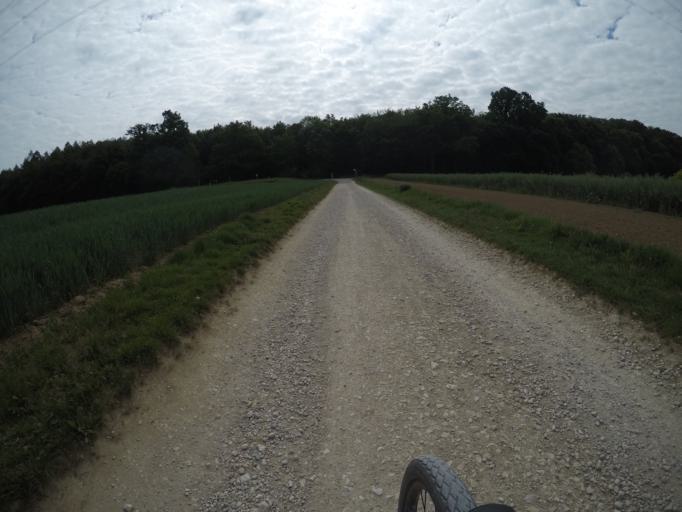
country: DE
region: Baden-Wuerttemberg
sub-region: Regierungsbezirk Stuttgart
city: Oberboihingen
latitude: 48.6503
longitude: 9.3939
